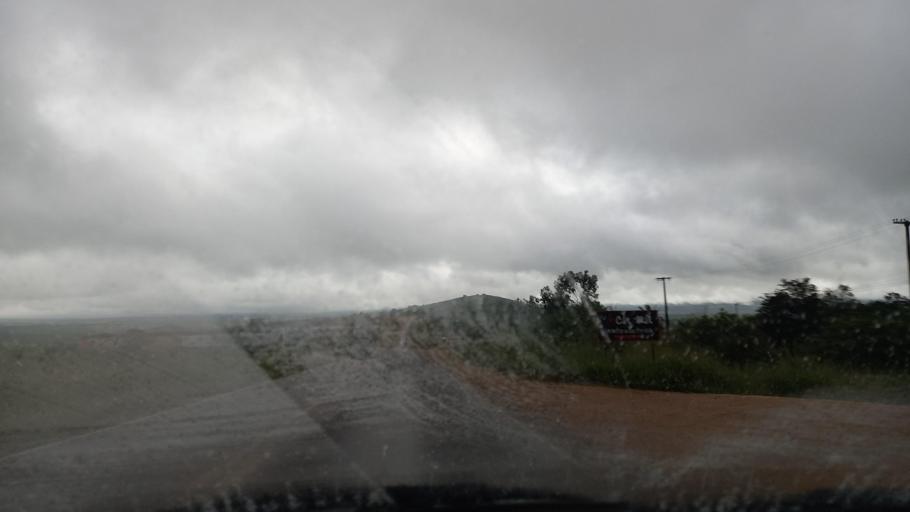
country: BR
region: Pernambuco
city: Garanhuns
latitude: -8.8675
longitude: -36.5086
